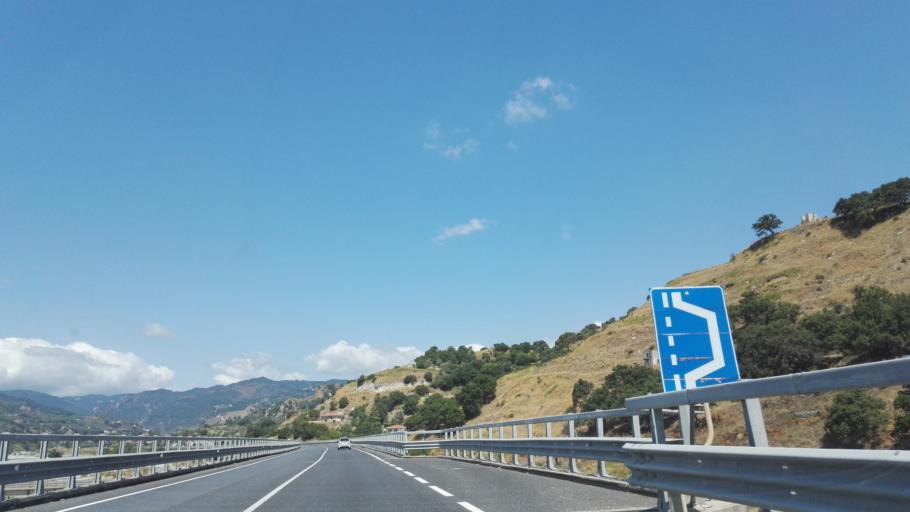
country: IT
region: Calabria
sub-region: Provincia di Reggio Calabria
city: Martone
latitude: 38.3398
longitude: 16.2777
